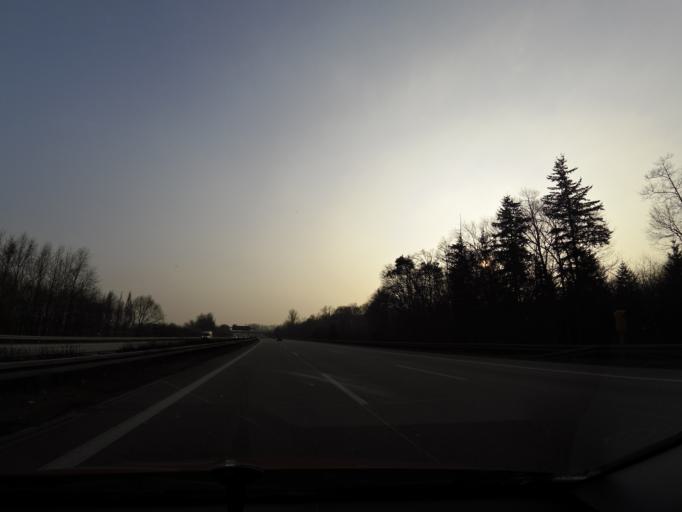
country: DE
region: Baden-Wuerttemberg
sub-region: Karlsruhe Region
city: Sinzheim
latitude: 48.7871
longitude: 8.1536
